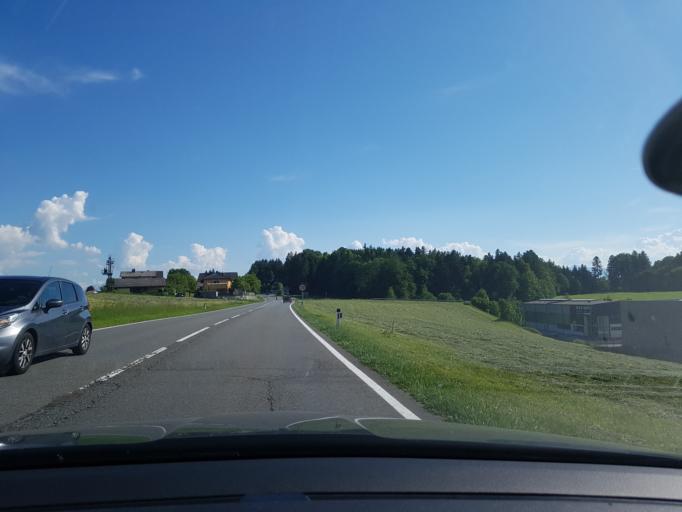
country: AT
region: Salzburg
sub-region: Politischer Bezirk Salzburg-Umgebung
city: Obertrum am See
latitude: 47.9123
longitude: 13.0824
